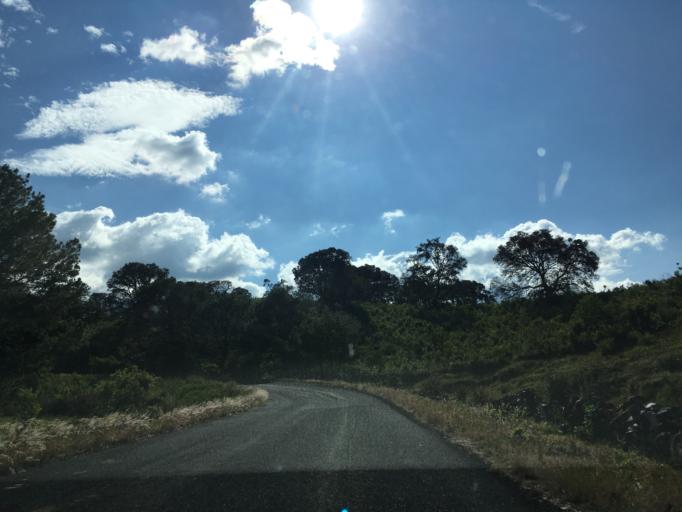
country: MX
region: Michoacan
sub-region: Zacapu
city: Naranja de Tapia
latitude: 19.7579
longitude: -101.7800
